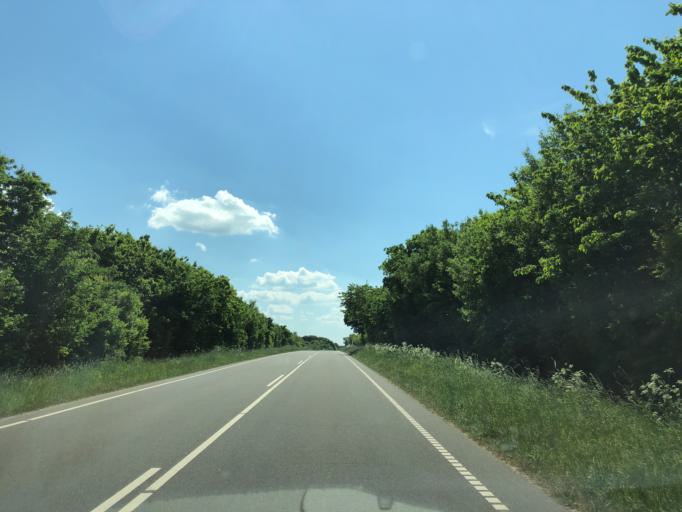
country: DK
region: Central Jutland
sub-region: Struer Kommune
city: Struer
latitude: 56.4823
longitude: 8.5551
